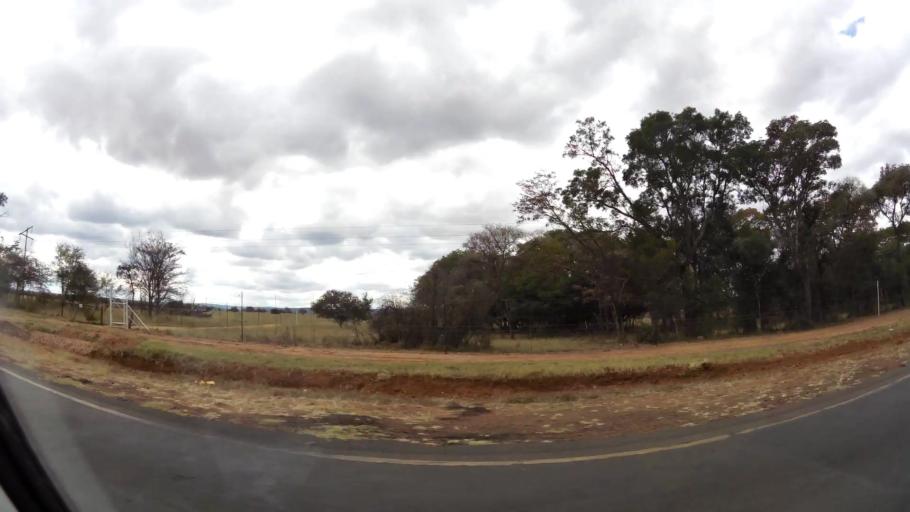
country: ZA
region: Limpopo
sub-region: Waterberg District Municipality
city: Modimolle
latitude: -24.7328
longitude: 28.4321
